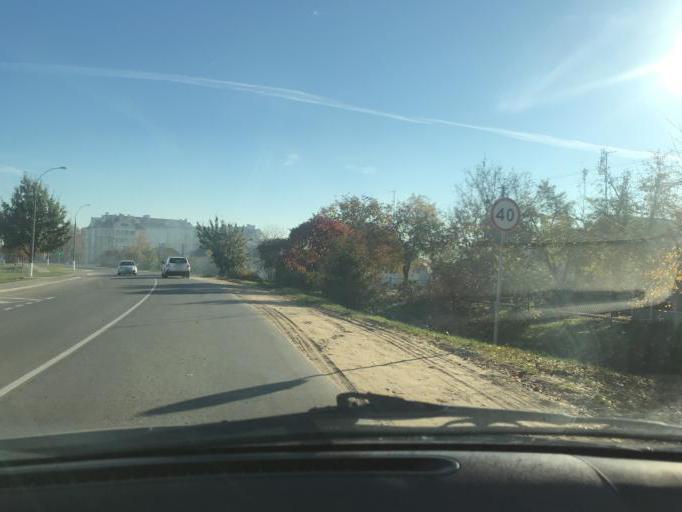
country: BY
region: Brest
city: Ivanava
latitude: 52.1430
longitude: 25.5225
